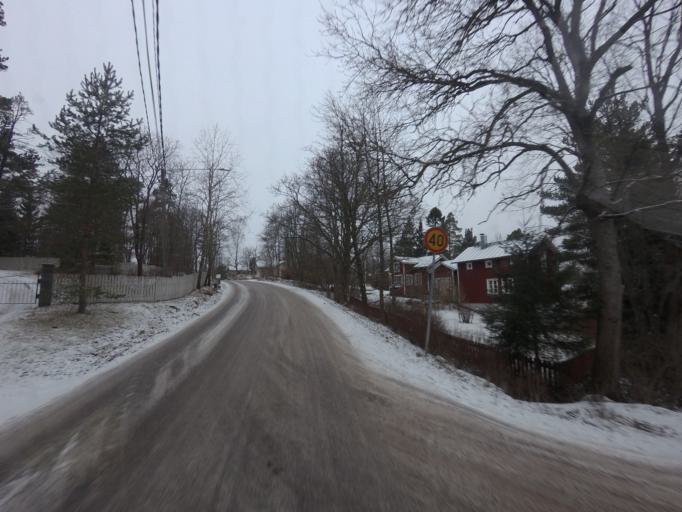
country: FI
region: Uusimaa
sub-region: Helsinki
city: Espoo
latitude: 60.1991
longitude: 24.5586
